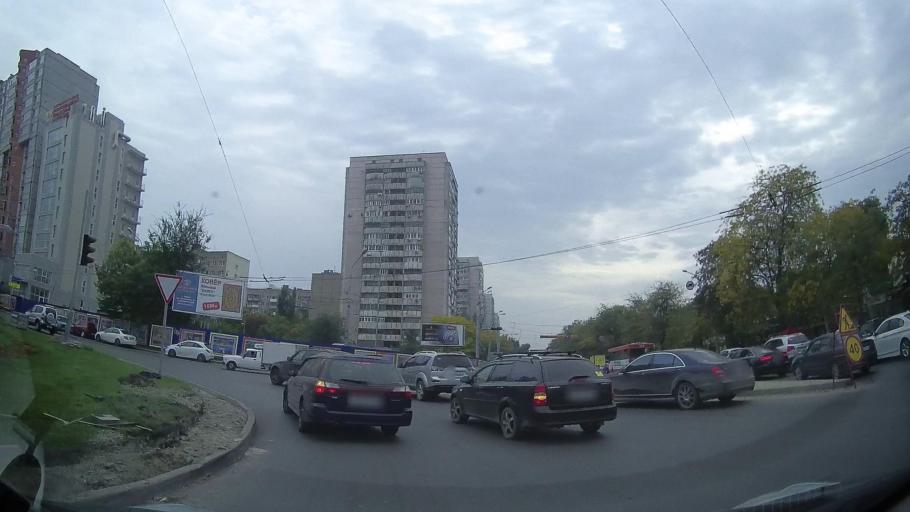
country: RU
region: Rostov
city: Rostov-na-Donu
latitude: 47.2357
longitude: 39.7129
